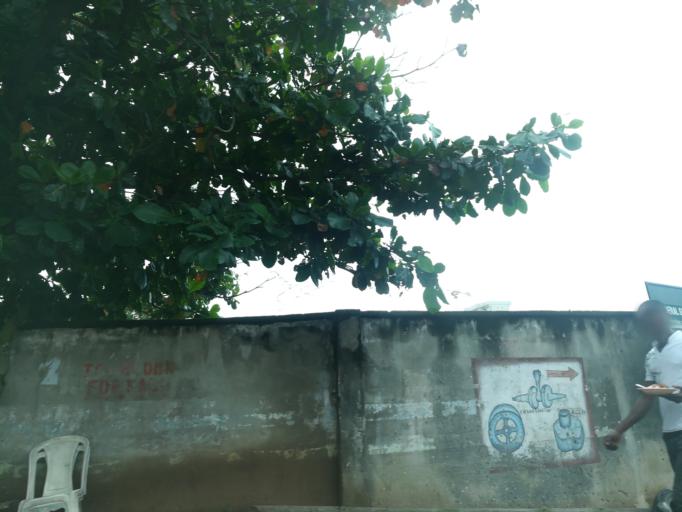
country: NG
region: Lagos
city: Lagos
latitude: 6.4220
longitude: 3.4089
